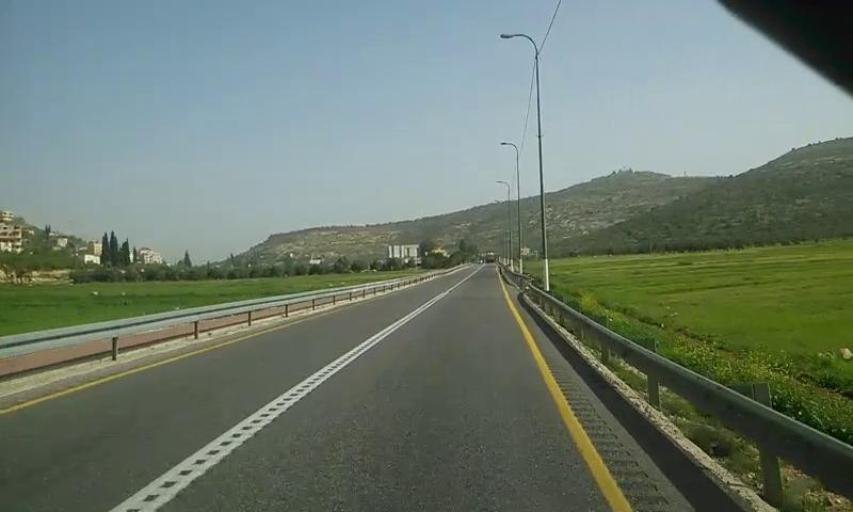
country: PS
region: West Bank
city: As Sawiyah
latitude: 32.0839
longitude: 35.2642
